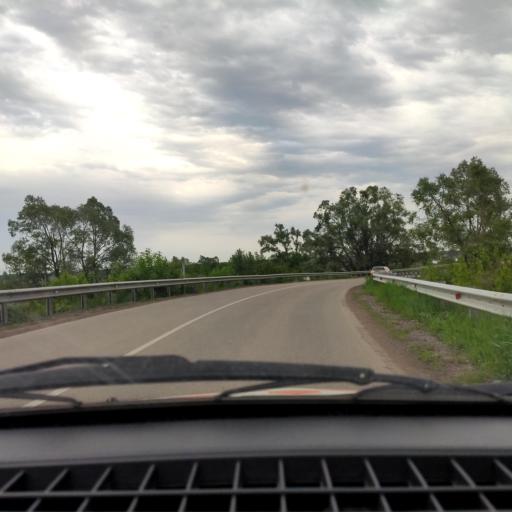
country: RU
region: Bashkortostan
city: Avdon
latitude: 54.5589
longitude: 55.7636
